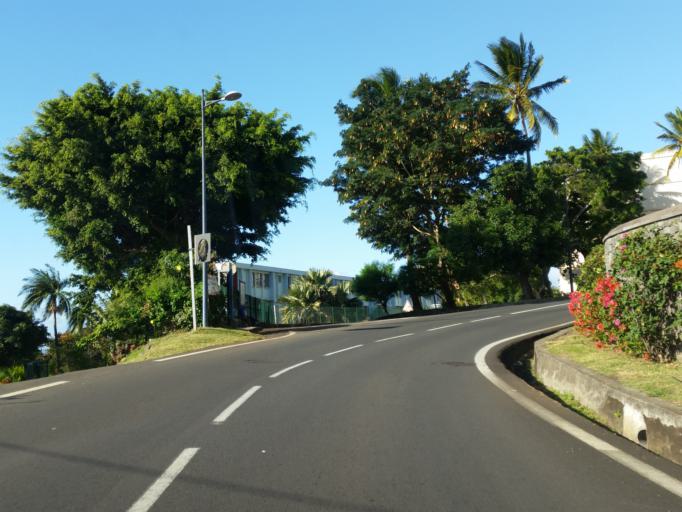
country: RE
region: Reunion
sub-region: Reunion
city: Saint-Denis
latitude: -20.8991
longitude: 55.4611
